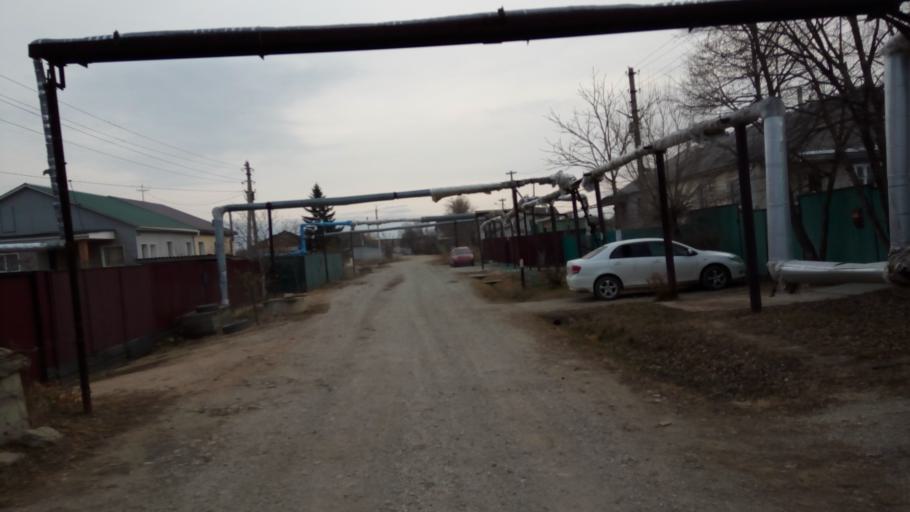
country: RU
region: Primorskiy
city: Novoshakhtinskiy
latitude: 44.0245
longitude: 132.1776
